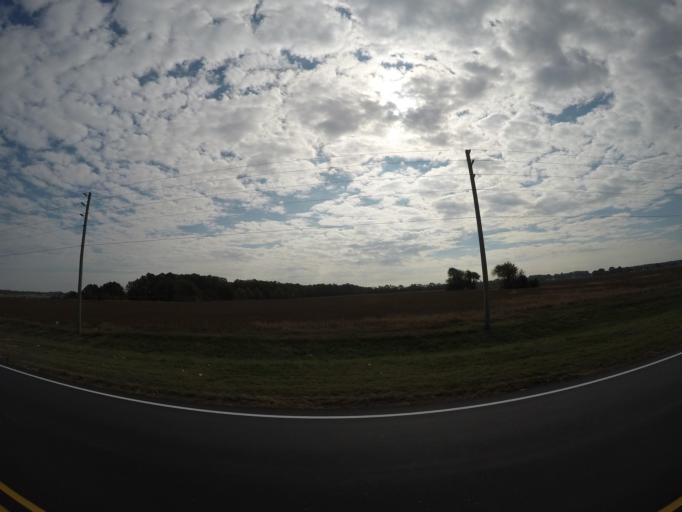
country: US
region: Delaware
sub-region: Sussex County
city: Bridgeville
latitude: 38.7591
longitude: -75.6208
